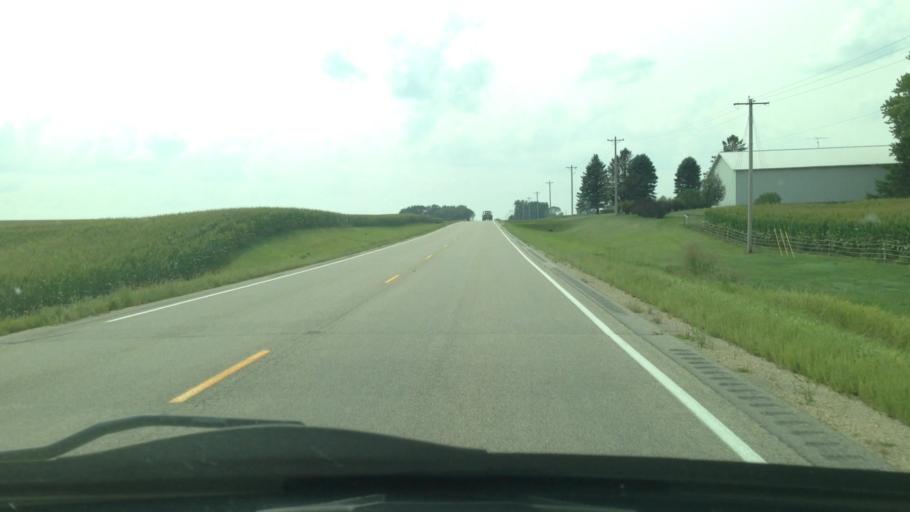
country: US
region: Minnesota
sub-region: Wabasha County
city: Elgin
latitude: 44.1655
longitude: -92.2797
